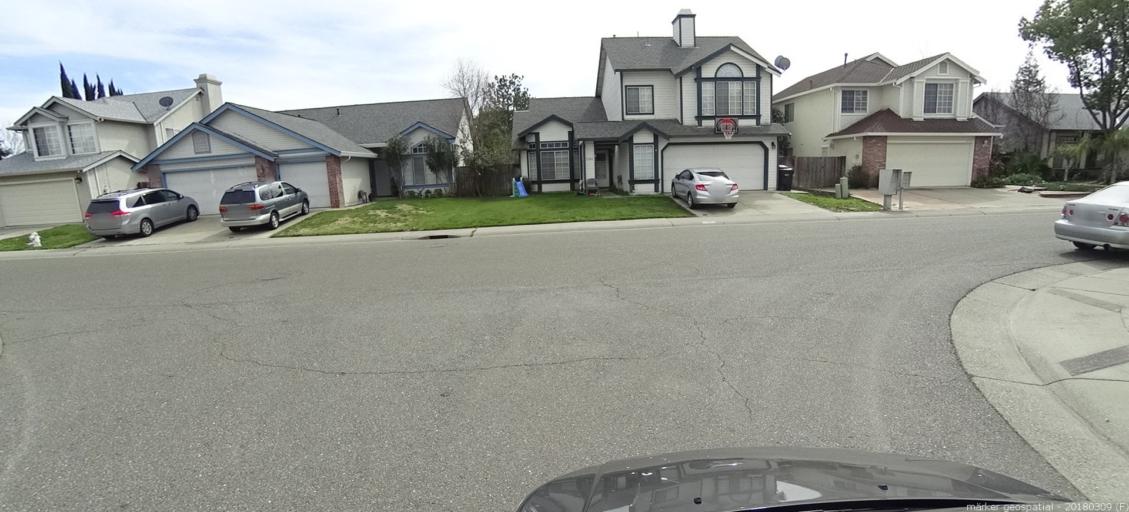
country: US
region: California
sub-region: Sacramento County
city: Vineyard
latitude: 38.4590
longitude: -121.3772
